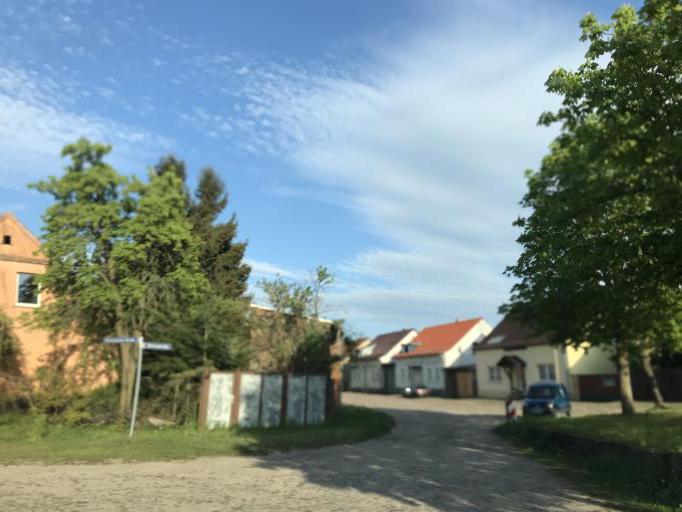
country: DE
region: Brandenburg
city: Joachimsthal
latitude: 52.9766
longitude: 13.7392
